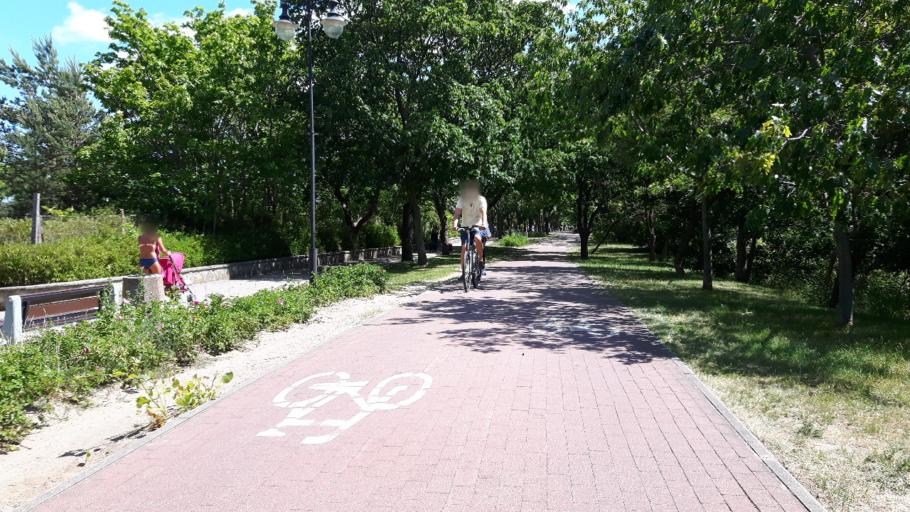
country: PL
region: Pomeranian Voivodeship
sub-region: Sopot
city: Sopot
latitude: 54.4288
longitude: 18.5924
